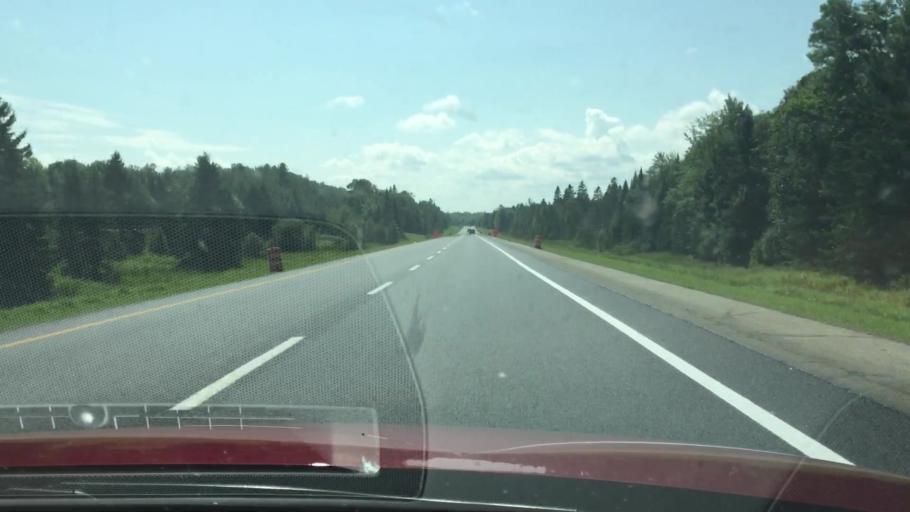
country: US
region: Maine
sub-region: Penobscot County
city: Patten
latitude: 45.8529
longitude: -68.4265
